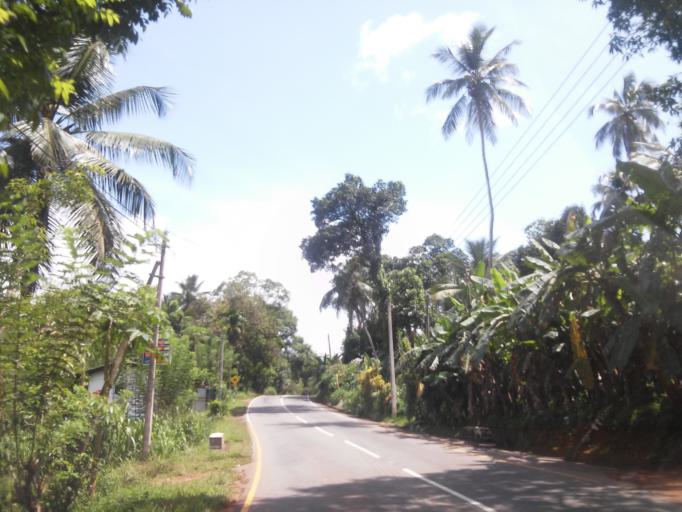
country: LK
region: Sabaragamuwa
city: Ratnapura
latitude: 6.7263
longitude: 80.3234
